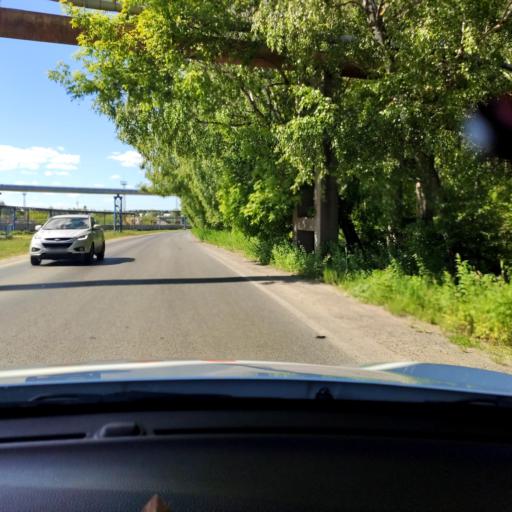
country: RU
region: Tatarstan
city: Staroye Arakchino
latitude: 55.8653
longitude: 48.9716
